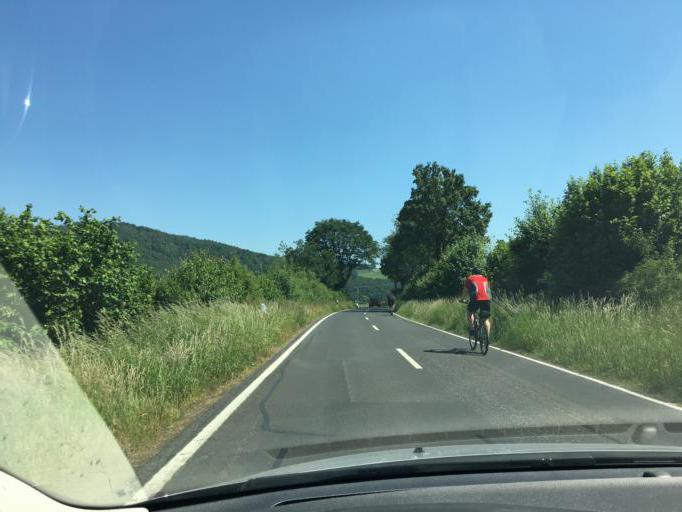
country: DE
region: Hesse
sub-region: Regierungsbezirk Kassel
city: Malsfeld
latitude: 51.0716
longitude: 9.5578
